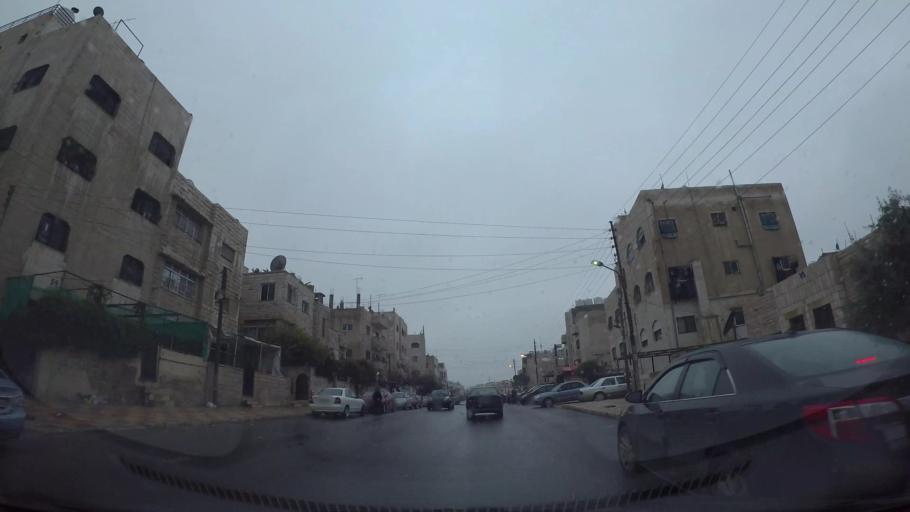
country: JO
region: Amman
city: Amman
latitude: 31.9732
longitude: 35.9210
